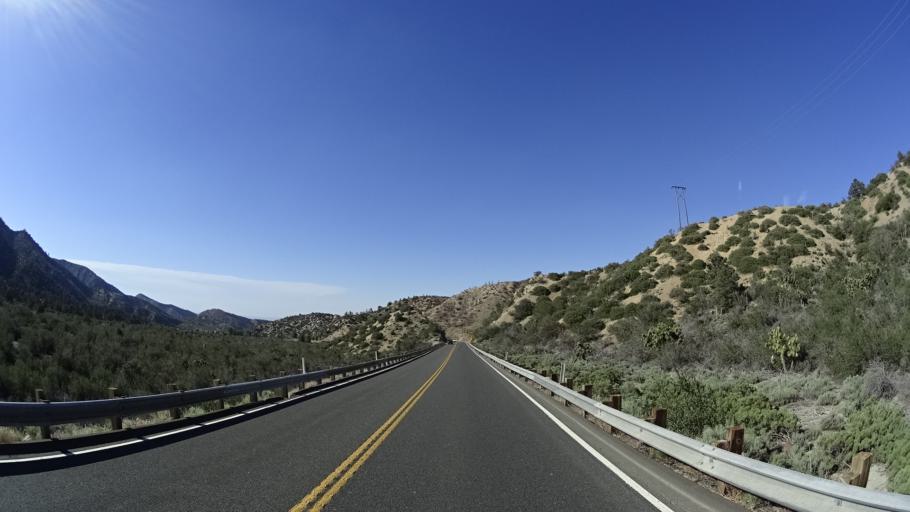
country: US
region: California
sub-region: San Bernardino County
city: Wrightwood
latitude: 34.3627
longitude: -117.6038
